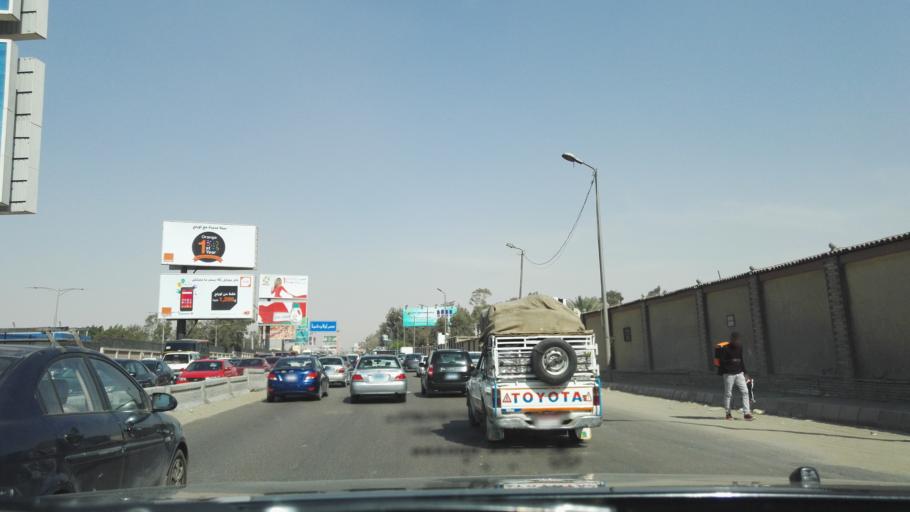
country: EG
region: Muhafazat al Qalyubiyah
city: Al Khankah
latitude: 30.0801
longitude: 31.3851
